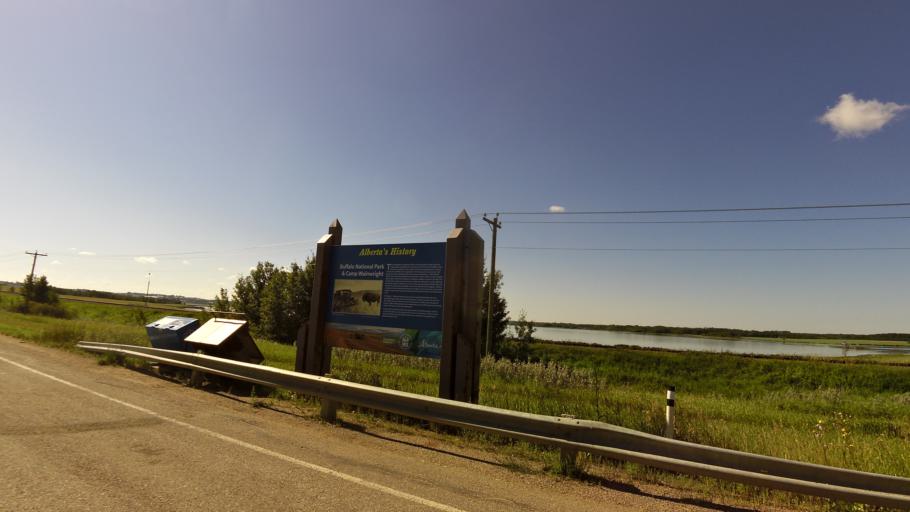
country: CA
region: Alberta
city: Wainwright
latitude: 52.8535
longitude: -110.9141
